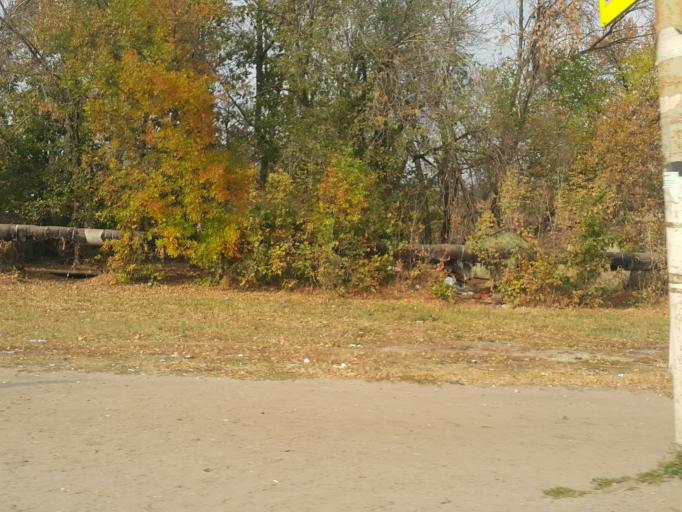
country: RU
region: Tambov
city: Bokino
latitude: 52.6516
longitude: 41.4446
